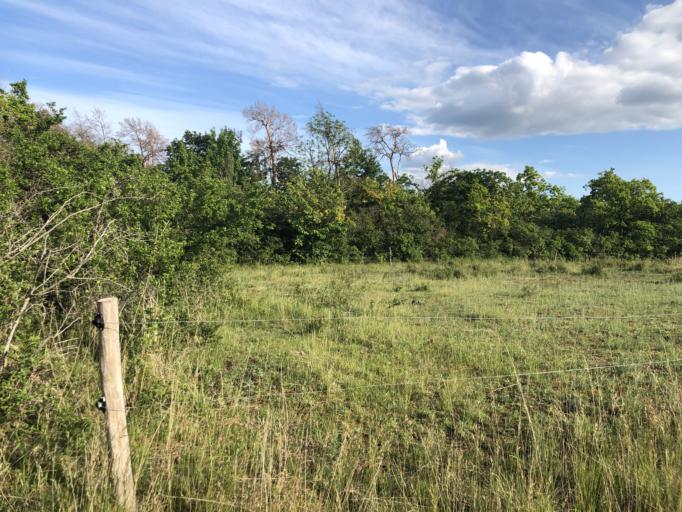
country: DE
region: Saxony-Anhalt
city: Freyburg
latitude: 51.2042
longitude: 11.7570
